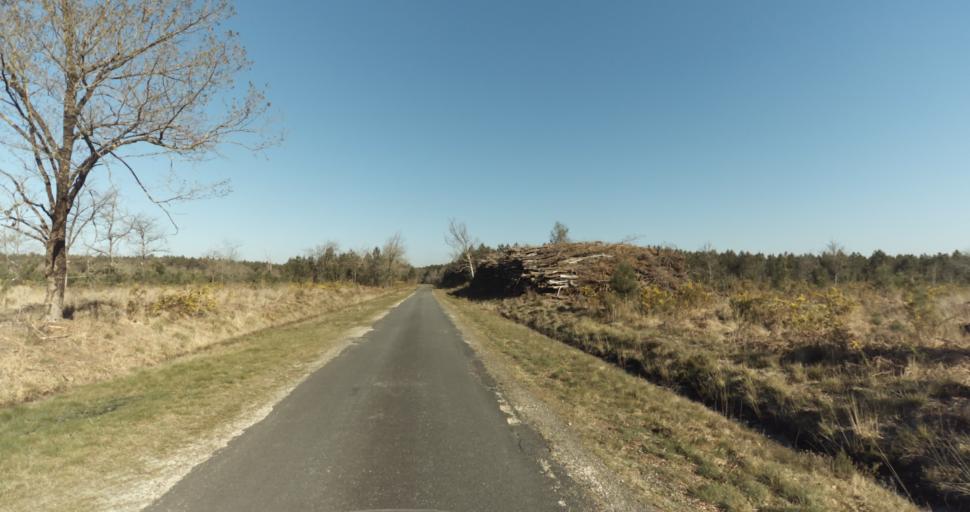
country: FR
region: Aquitaine
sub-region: Departement de la Gironde
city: Martignas-sur-Jalle
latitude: 44.8102
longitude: -0.8519
